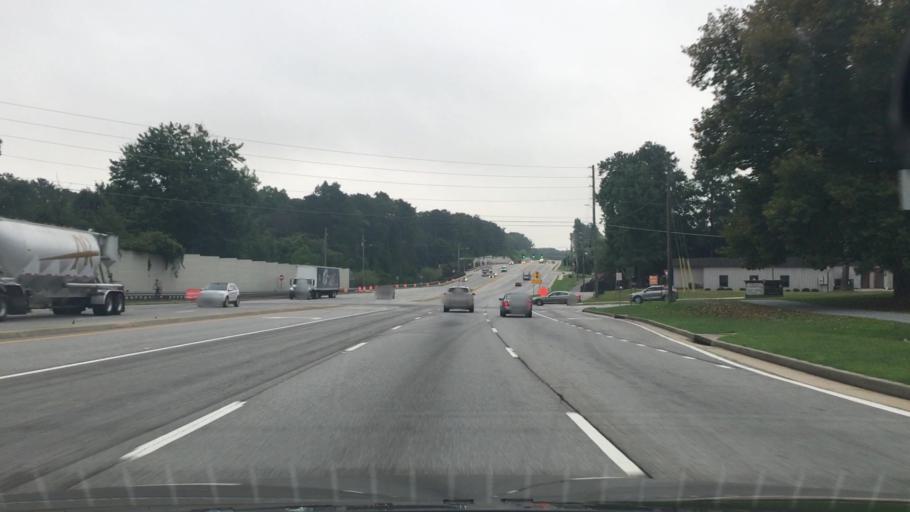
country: US
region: Georgia
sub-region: Fayette County
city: Peachtree City
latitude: 33.3942
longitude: -84.5869
